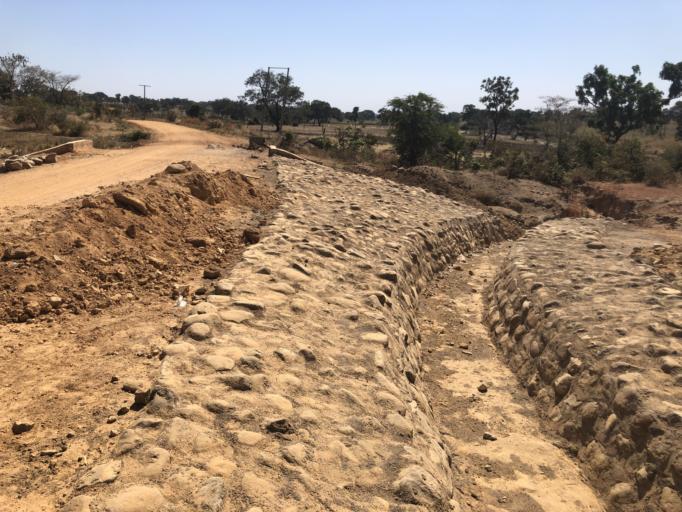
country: NG
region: Adamawa
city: Toungo
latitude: 8.1440
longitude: 11.9846
